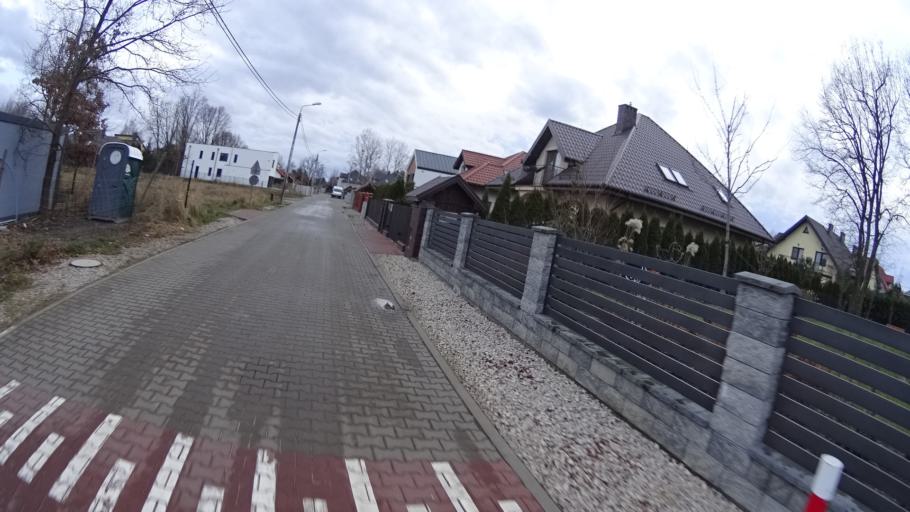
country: PL
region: Masovian Voivodeship
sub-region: Powiat pruszkowski
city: Granica
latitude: 52.1487
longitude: 20.7949
